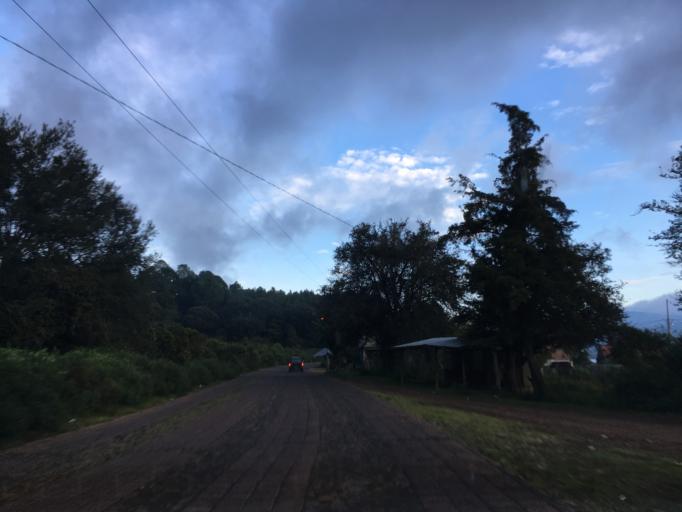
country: MX
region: Michoacan
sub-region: Patzcuaro
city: Santa Maria Huiramangaro (San Juan Tumbio)
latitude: 19.4417
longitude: -101.7227
